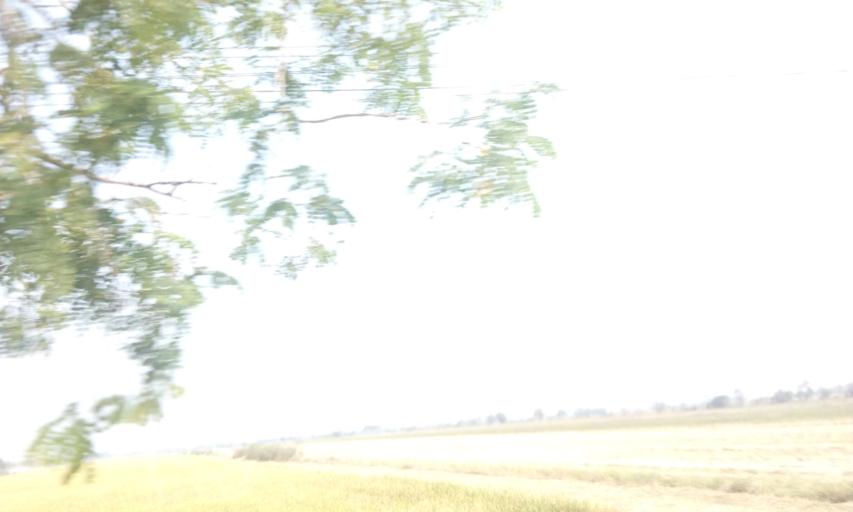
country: TH
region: Pathum Thani
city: Ban Rangsit
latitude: 14.0091
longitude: 100.7576
